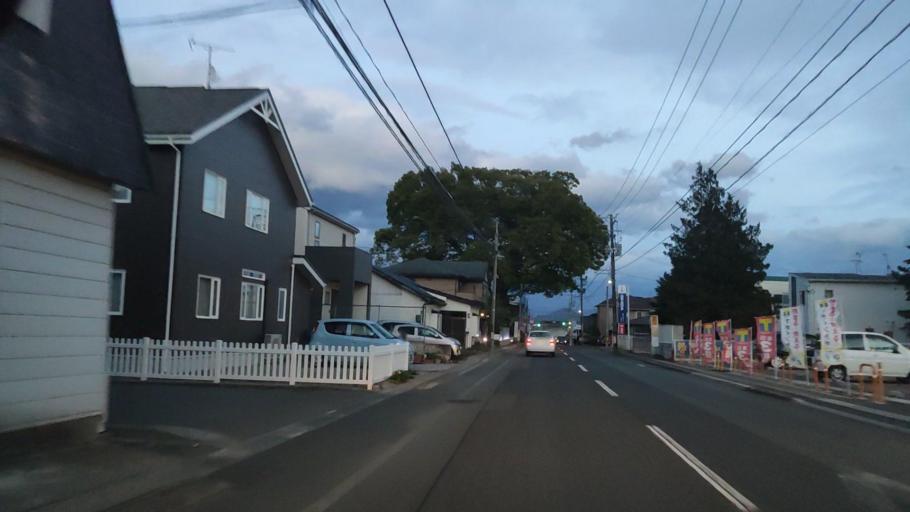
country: JP
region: Iwate
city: Morioka-shi
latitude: 39.7172
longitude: 141.1236
